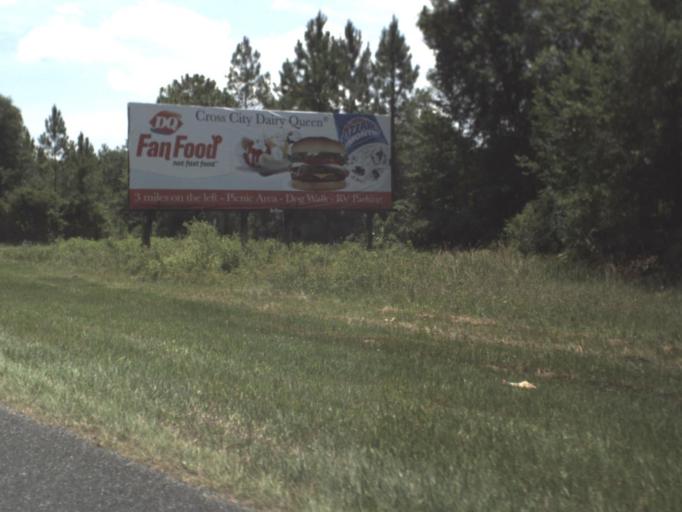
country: US
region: Florida
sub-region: Dixie County
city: Cross City
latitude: 29.6538
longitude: -83.1763
